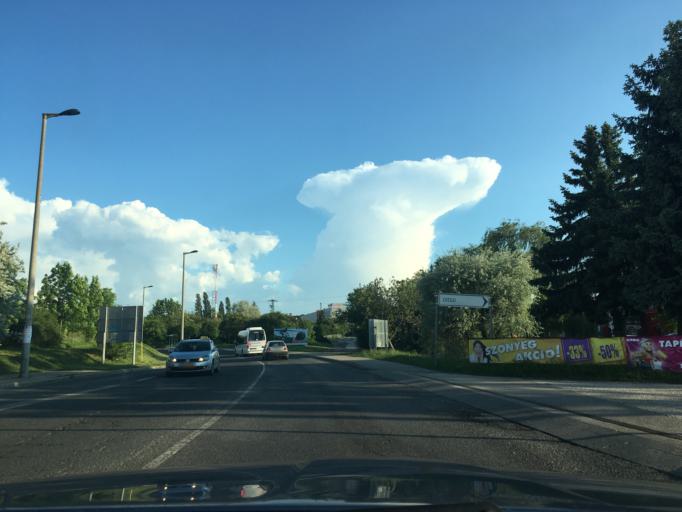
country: HU
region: Pest
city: Budaors
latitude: 47.4503
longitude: 18.9623
